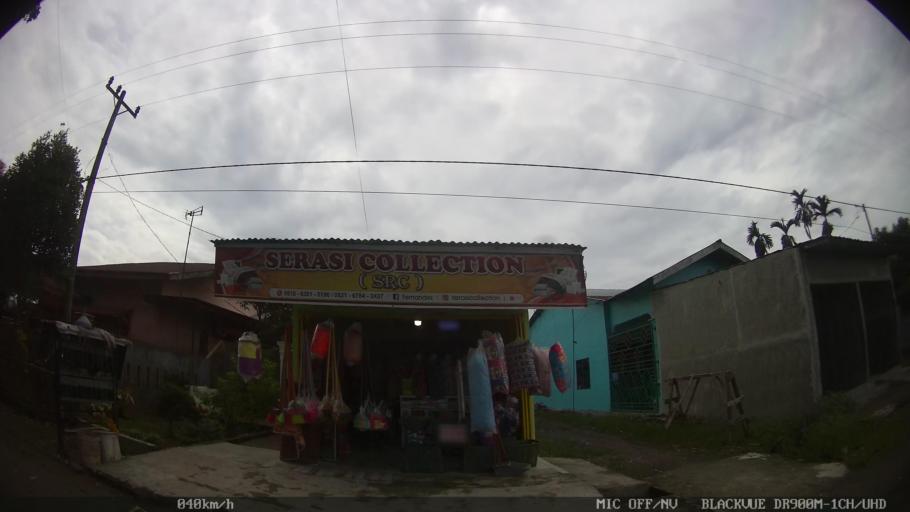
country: ID
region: North Sumatra
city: Sunggal
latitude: 3.5820
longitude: 98.5651
